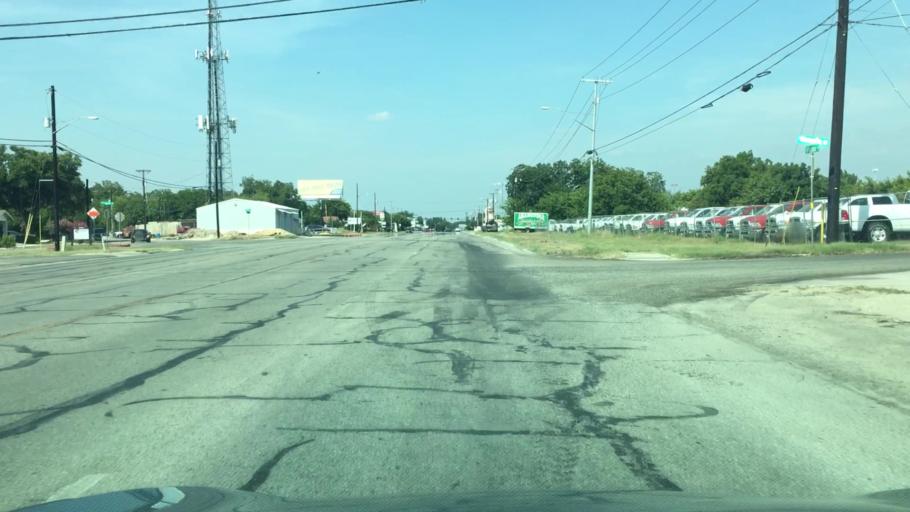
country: US
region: Texas
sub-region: Comal County
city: New Braunfels
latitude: 29.6871
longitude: -98.1317
